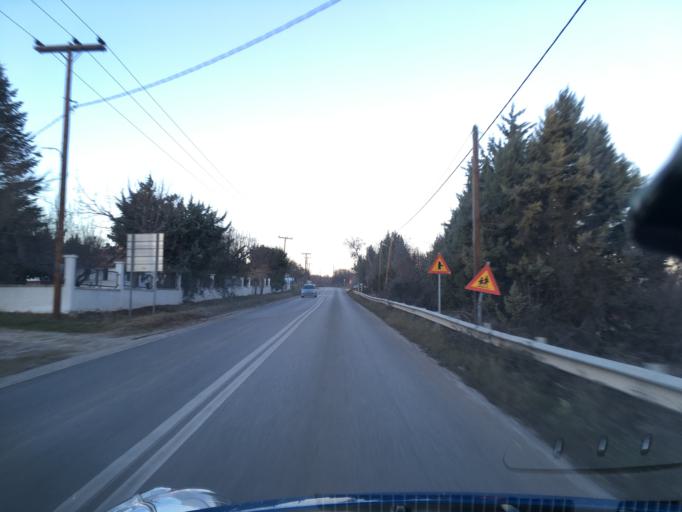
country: GR
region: West Macedonia
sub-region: Nomos Kozanis
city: Kozani
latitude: 40.2777
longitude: 21.7831
